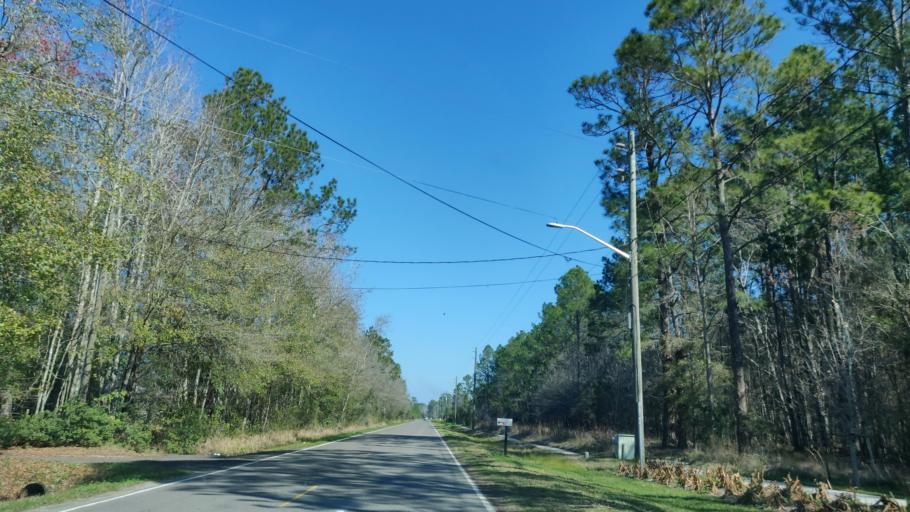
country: US
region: Florida
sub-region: Duval County
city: Baldwin
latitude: 30.1986
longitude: -81.9661
